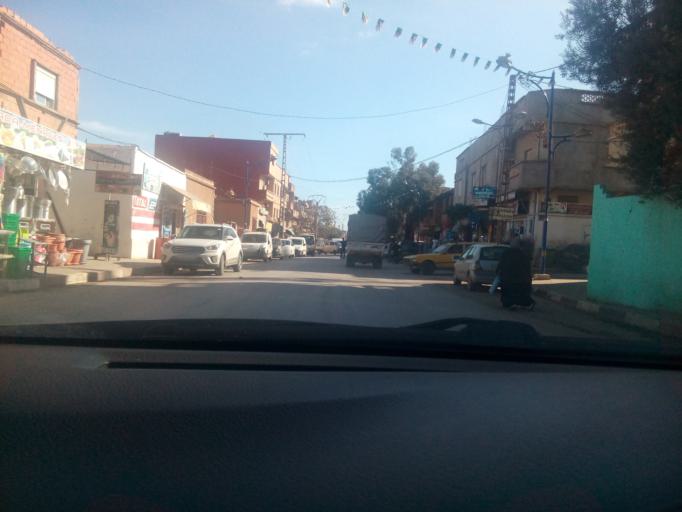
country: DZ
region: Oran
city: Es Senia
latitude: 35.6725
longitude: -0.5754
